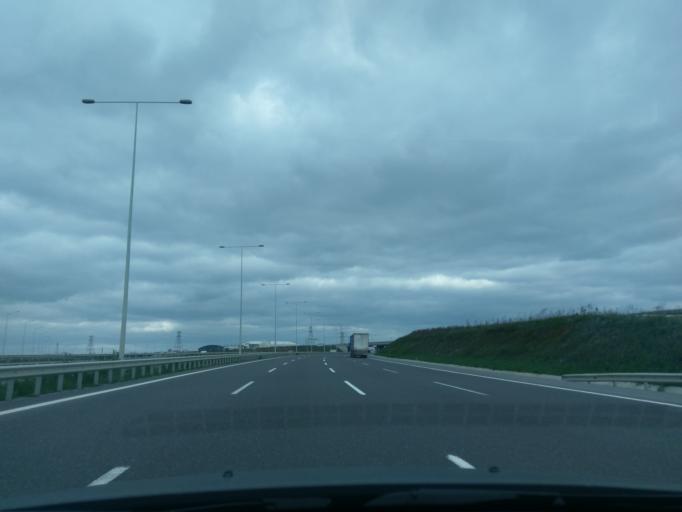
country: TR
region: Istanbul
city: Basaksehir
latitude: 41.1345
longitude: 28.8046
